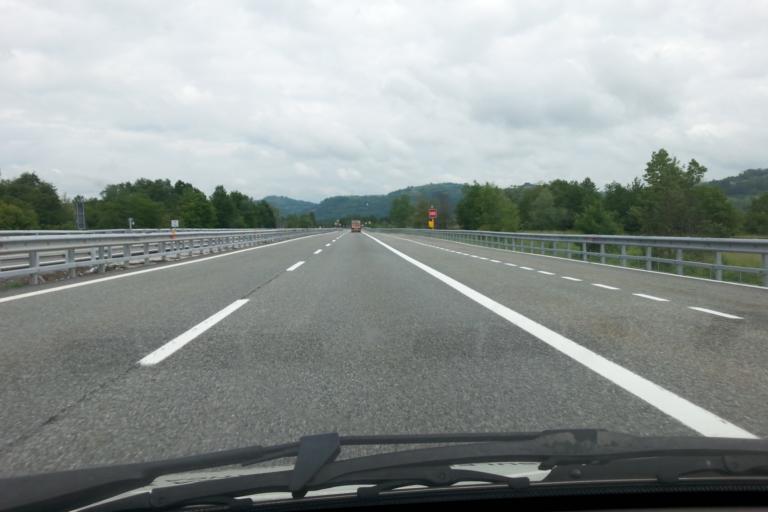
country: IT
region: Piedmont
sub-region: Provincia di Cuneo
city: Lesegno
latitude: 44.4053
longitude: 7.9711
